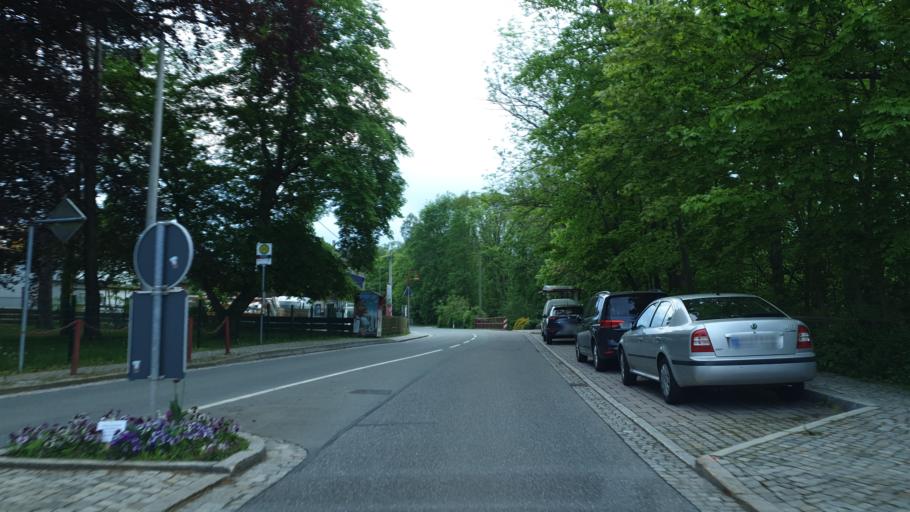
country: DE
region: Saxony
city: Lugau
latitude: 50.7197
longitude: 12.7473
